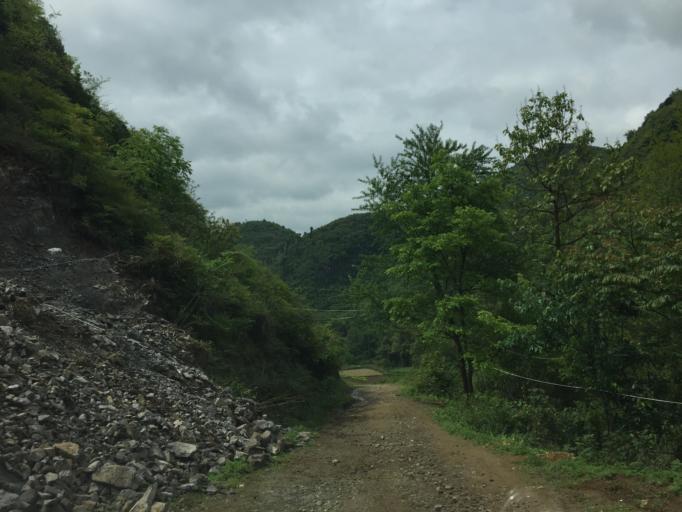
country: CN
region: Guizhou Sheng
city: Kuanping
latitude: 28.0084
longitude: 108.0674
